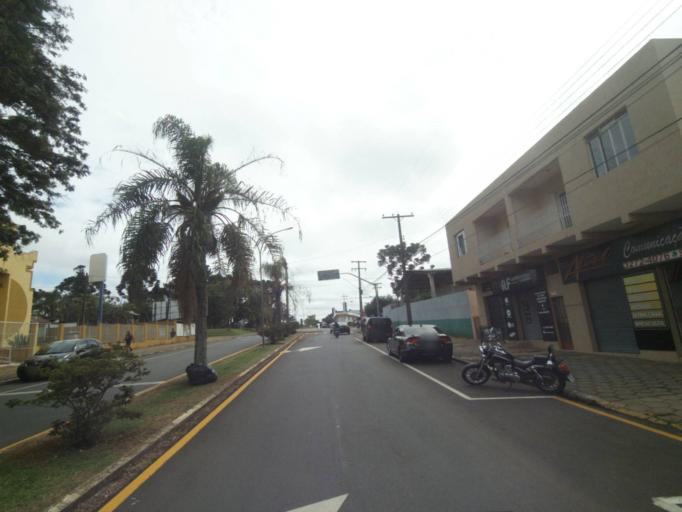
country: BR
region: Parana
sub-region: Telemaco Borba
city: Telemaco Borba
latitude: -24.3317
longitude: -50.6229
